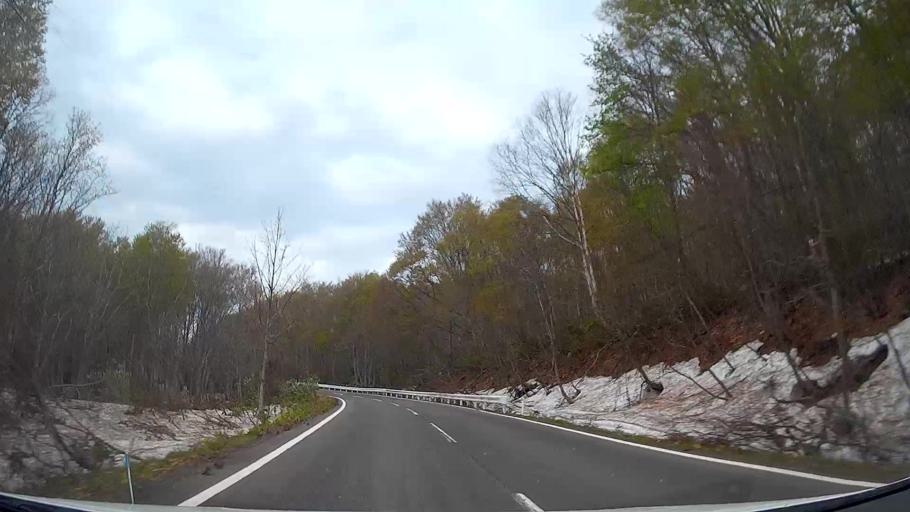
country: JP
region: Aomori
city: Aomori Shi
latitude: 40.6866
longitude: 140.8352
